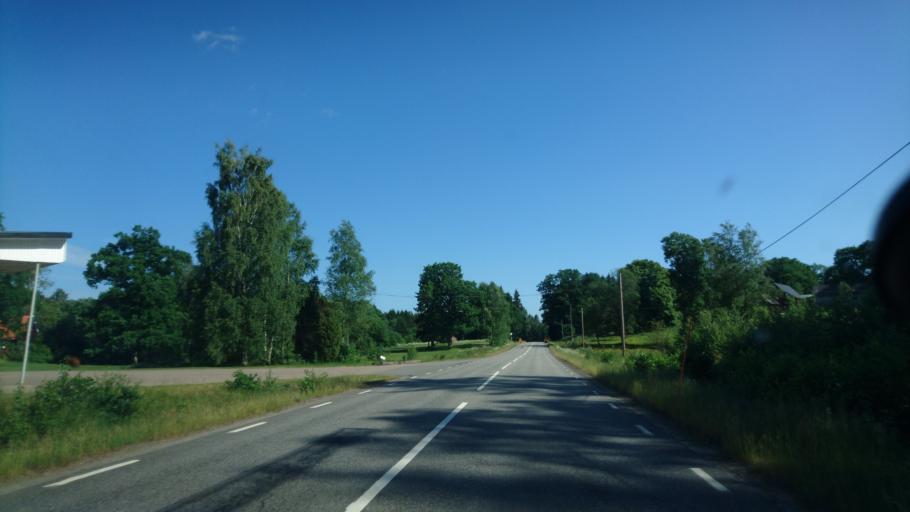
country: SE
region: Skane
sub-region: Osby Kommun
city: Lonsboda
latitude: 56.4225
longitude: 14.2834
